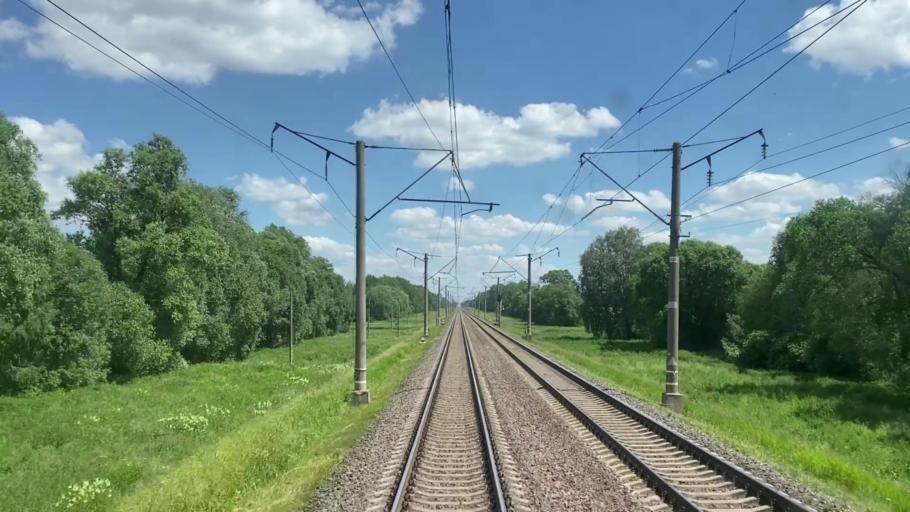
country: BY
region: Brest
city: Pruzhany
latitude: 52.5046
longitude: 24.6505
